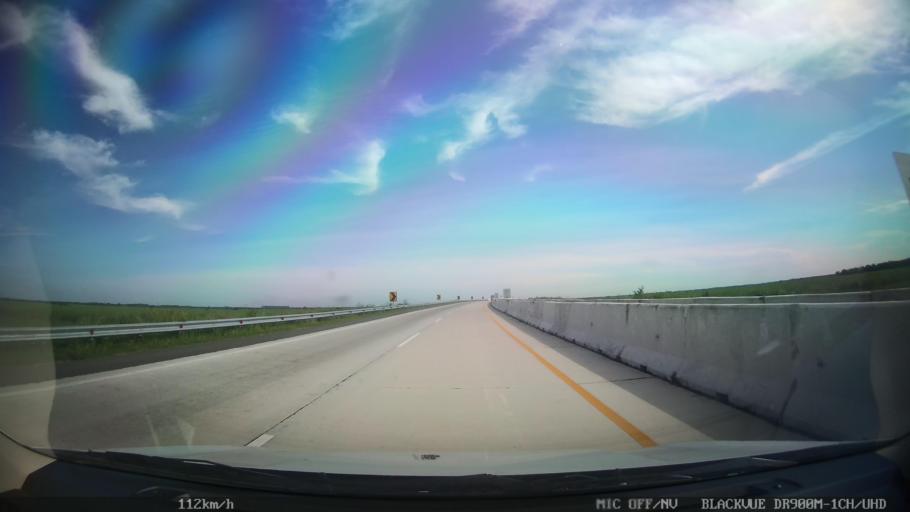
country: ID
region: North Sumatra
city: Binjai
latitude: 3.6617
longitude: 98.5324
